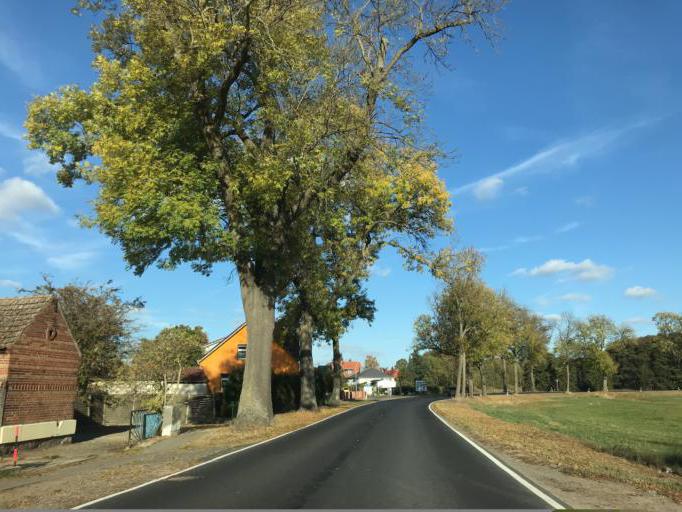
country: DE
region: Brandenburg
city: Schonermark
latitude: 53.0084
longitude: 13.1290
